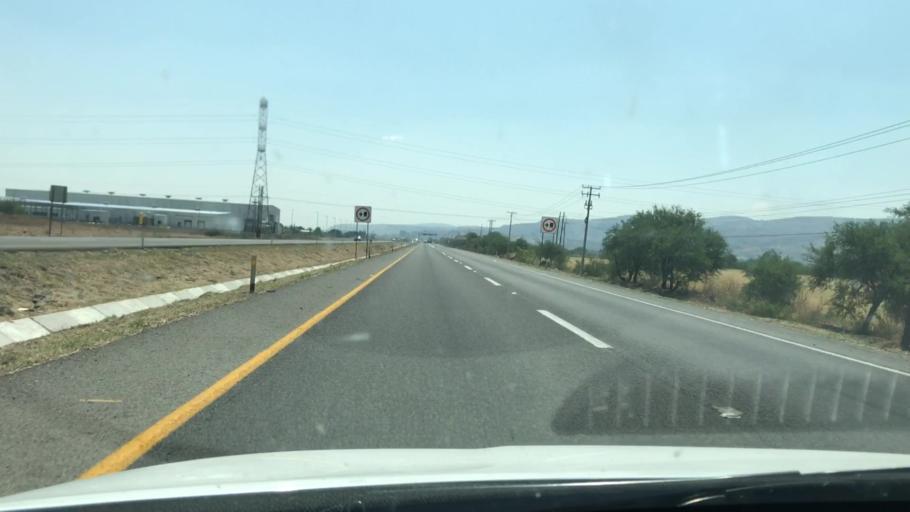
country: MX
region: Guanajuato
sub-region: Penjamo
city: Estacion Corralejo
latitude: 20.4517
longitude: -101.5782
